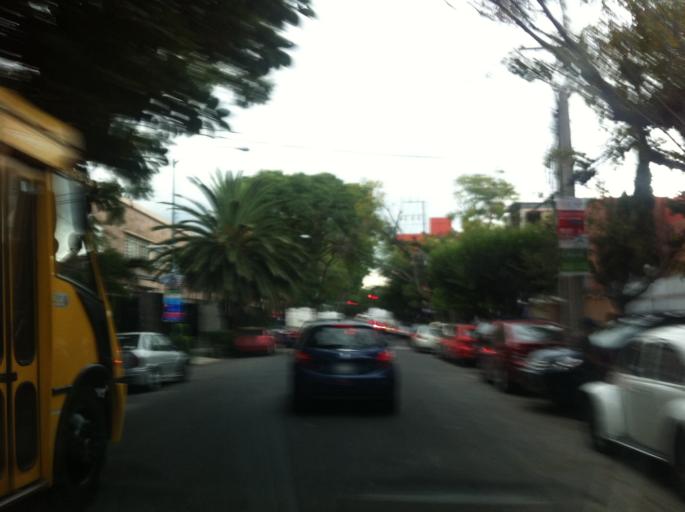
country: MX
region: Mexico City
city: Colonia del Valle
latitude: 19.3836
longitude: -99.1634
